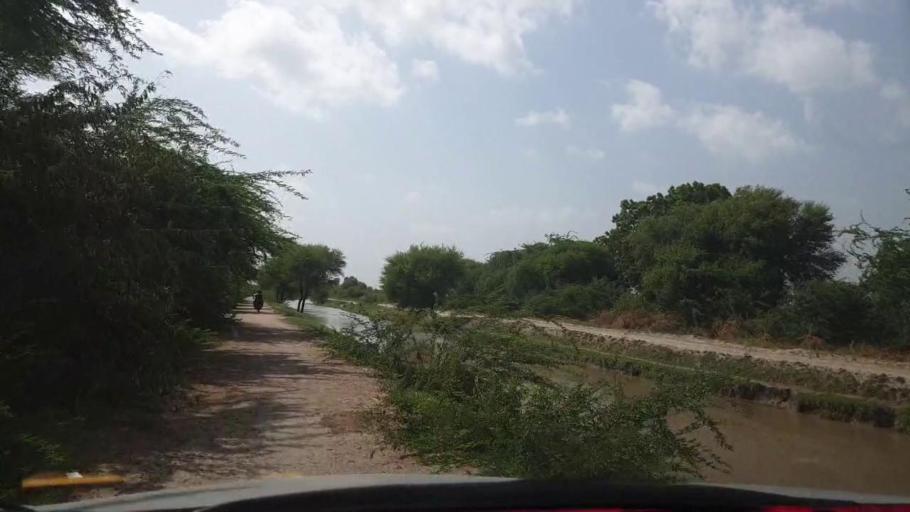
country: PK
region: Sindh
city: Talhar
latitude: 24.8602
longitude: 68.9059
